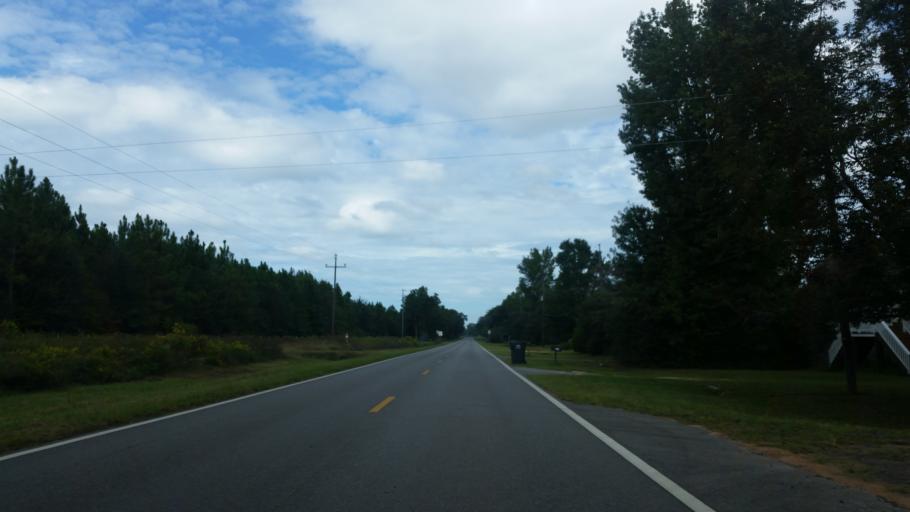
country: US
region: Florida
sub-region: Santa Rosa County
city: Point Baker
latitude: 30.6937
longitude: -86.9933
